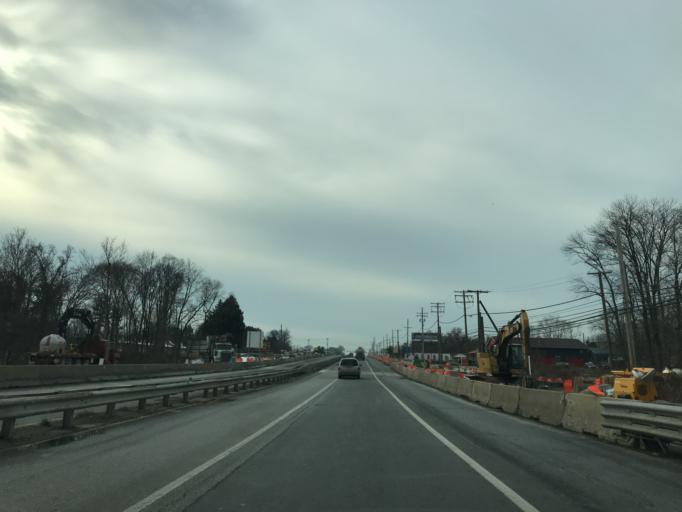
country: US
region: Maryland
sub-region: Harford County
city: Perryman
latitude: 39.4912
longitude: -76.1911
